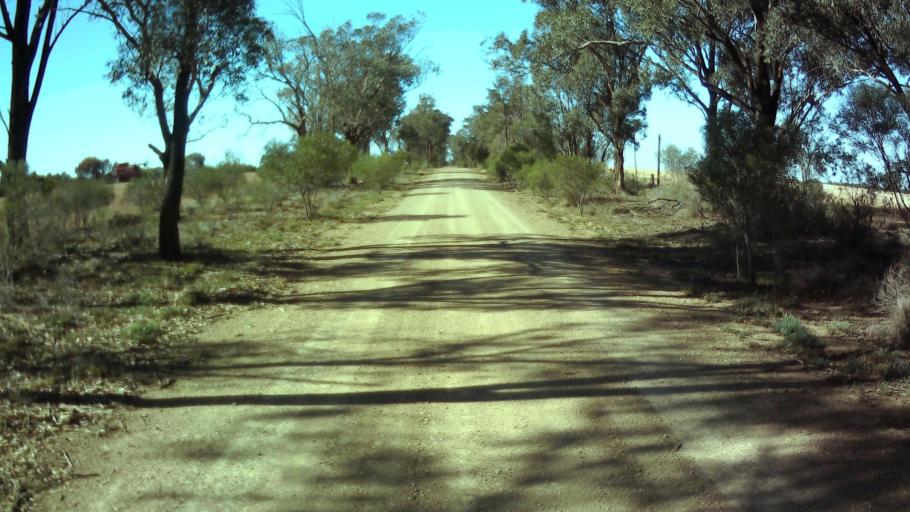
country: AU
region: New South Wales
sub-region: Weddin
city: Grenfell
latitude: -33.9055
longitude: 147.8777
